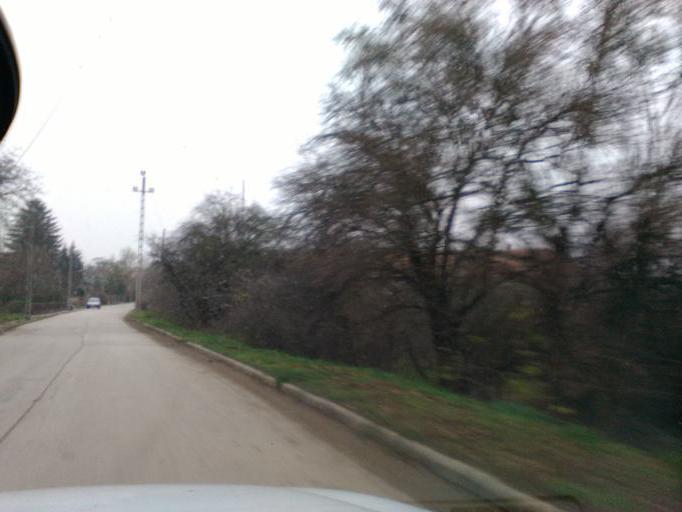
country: HU
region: Pest
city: Soskut
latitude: 47.4018
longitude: 18.7850
